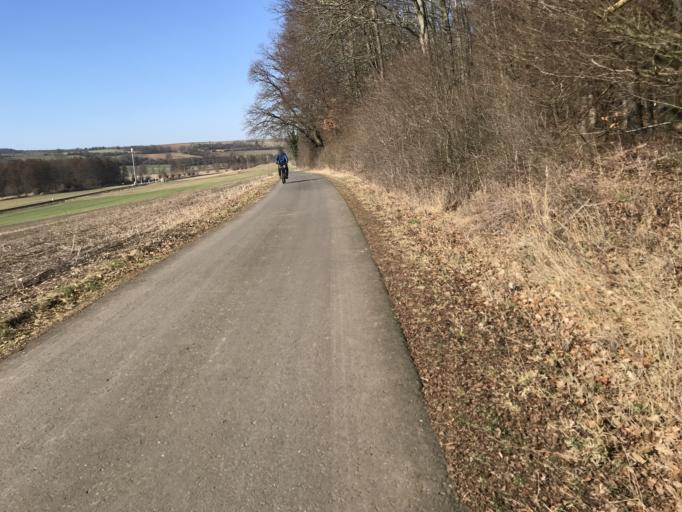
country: DE
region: Hesse
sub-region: Regierungsbezirk Darmstadt
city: Ranstadt
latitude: 50.3844
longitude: 8.9828
